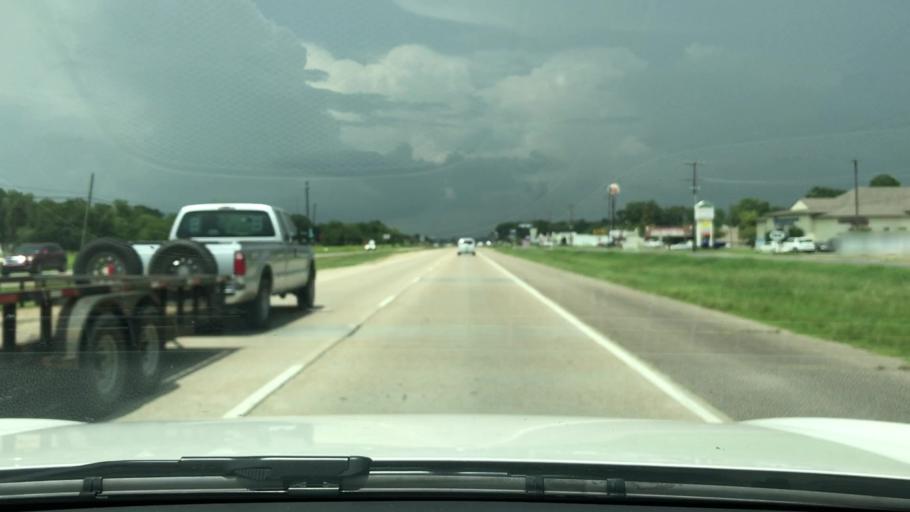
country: US
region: Louisiana
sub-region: West Baton Rouge Parish
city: Brusly
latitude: 30.4049
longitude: -91.2313
